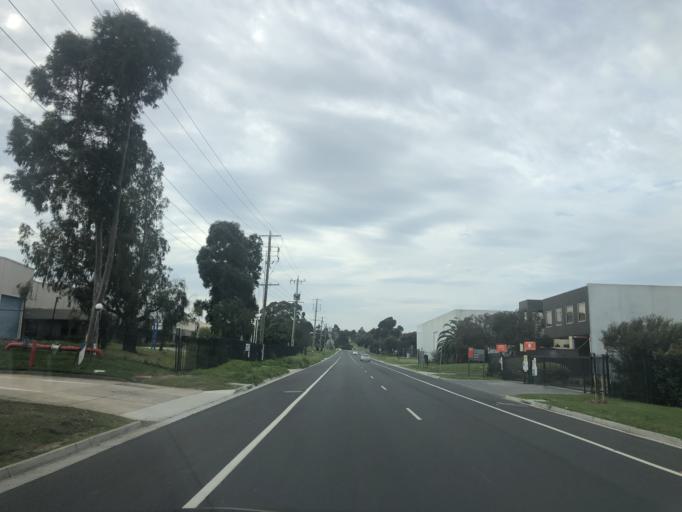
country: AU
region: Victoria
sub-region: Casey
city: Hallam
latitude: -38.0094
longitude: 145.2556
